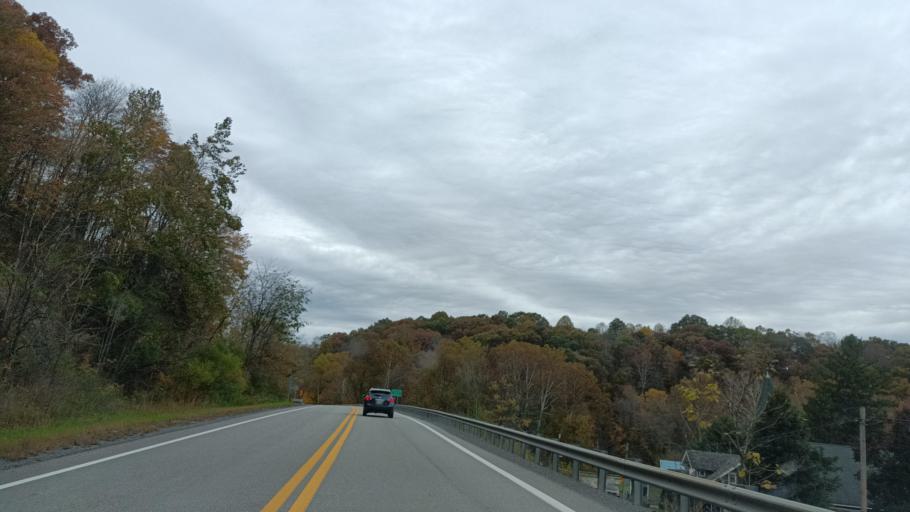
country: US
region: West Virginia
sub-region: Taylor County
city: Grafton
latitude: 39.3450
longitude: -79.9400
